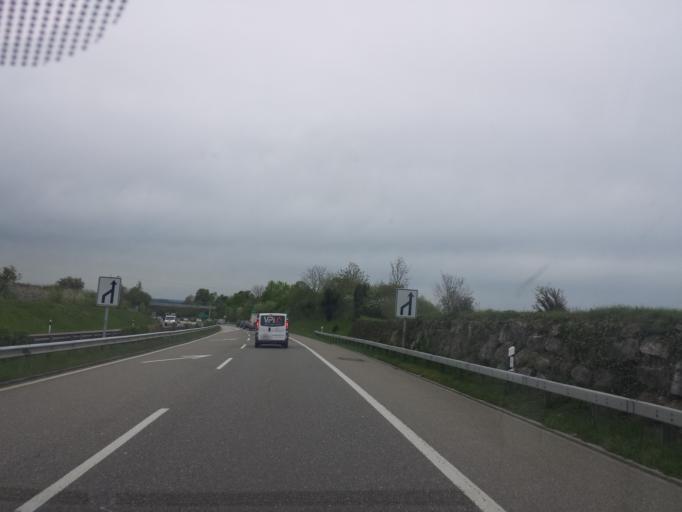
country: CH
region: Saint Gallen
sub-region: Wahlkreis Rorschach
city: Horn
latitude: 47.4861
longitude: 9.4399
